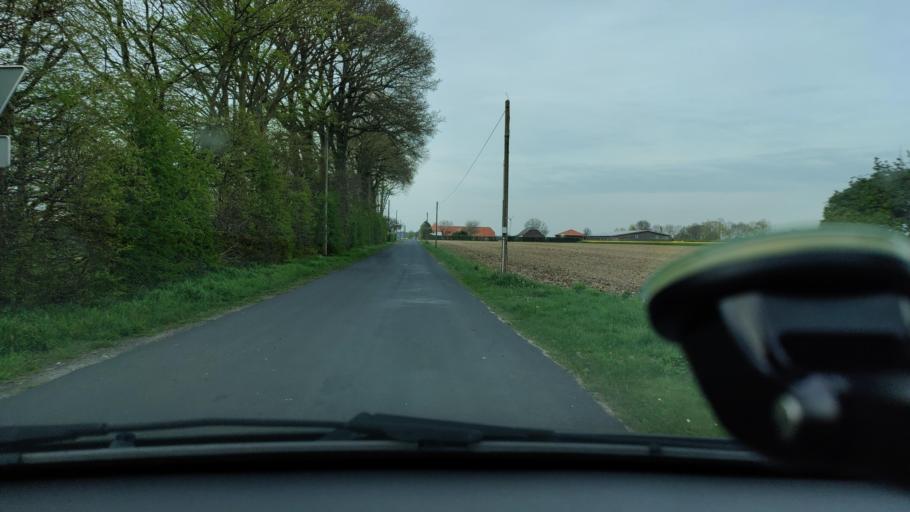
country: DE
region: North Rhine-Westphalia
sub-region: Regierungsbezirk Dusseldorf
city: Goch
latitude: 51.7043
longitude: 6.1775
